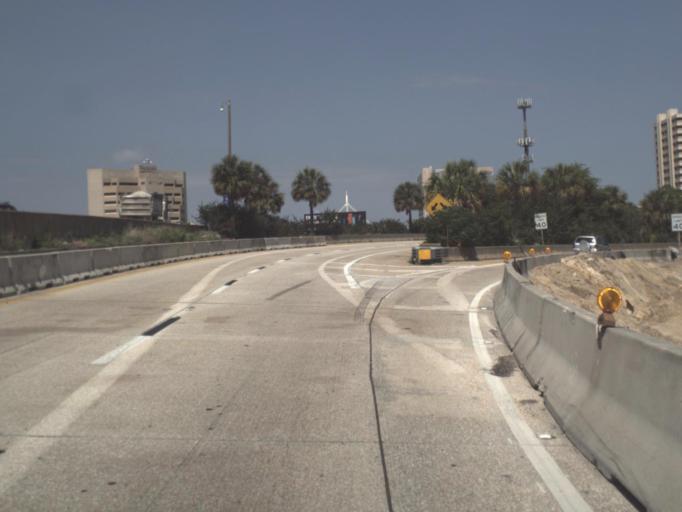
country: US
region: Florida
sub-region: Duval County
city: Jacksonville
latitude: 30.3143
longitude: -81.6575
